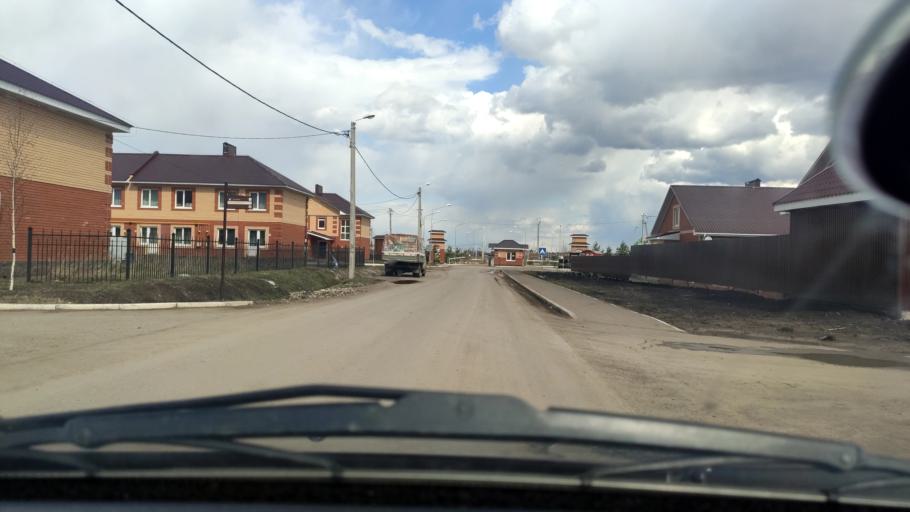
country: RU
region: Bashkortostan
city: Ufa
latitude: 54.6208
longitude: 55.8854
